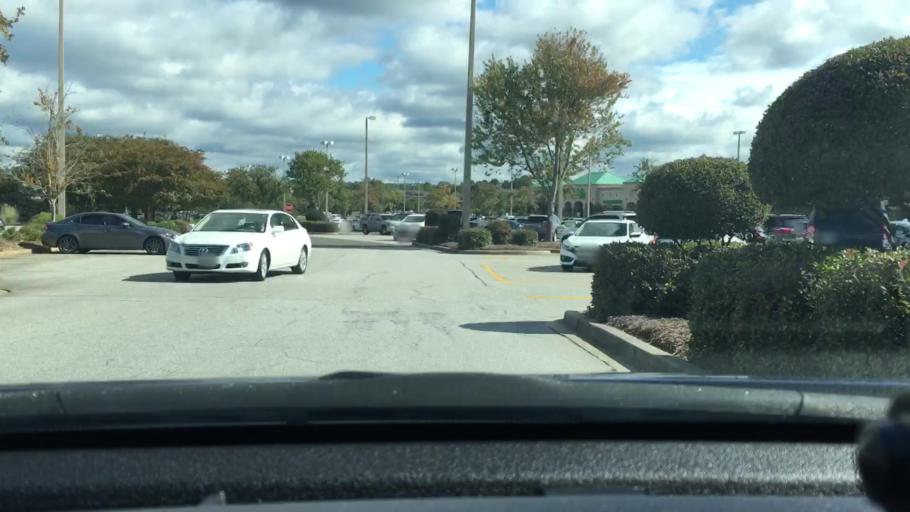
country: US
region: South Carolina
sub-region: Lexington County
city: Irmo
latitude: 34.0677
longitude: -81.1645
